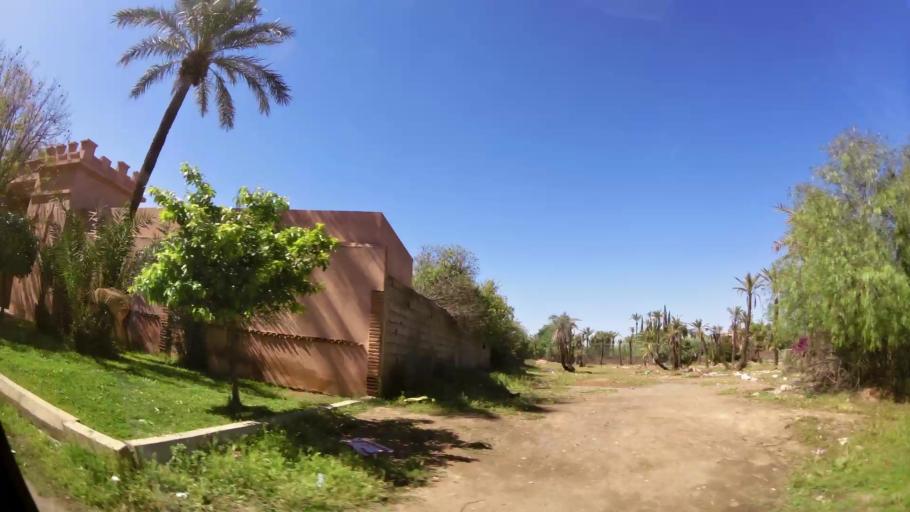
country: MA
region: Marrakech-Tensift-Al Haouz
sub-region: Marrakech
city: Marrakesh
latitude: 31.6537
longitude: -7.9613
